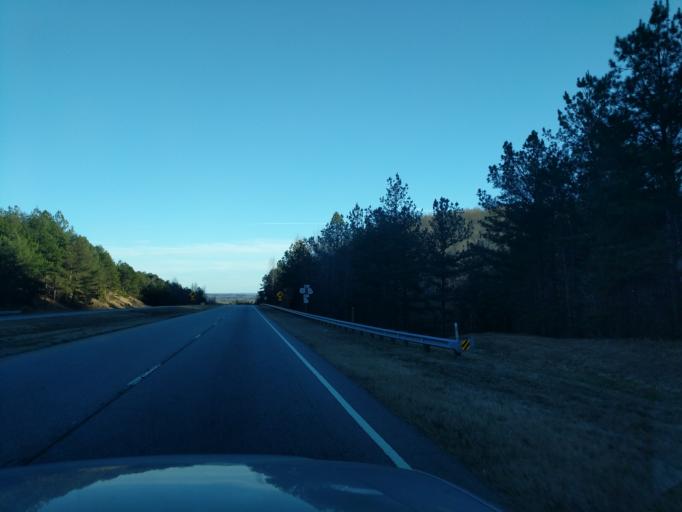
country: US
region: Georgia
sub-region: Stephens County
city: Toccoa
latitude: 34.5587
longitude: -83.3882
